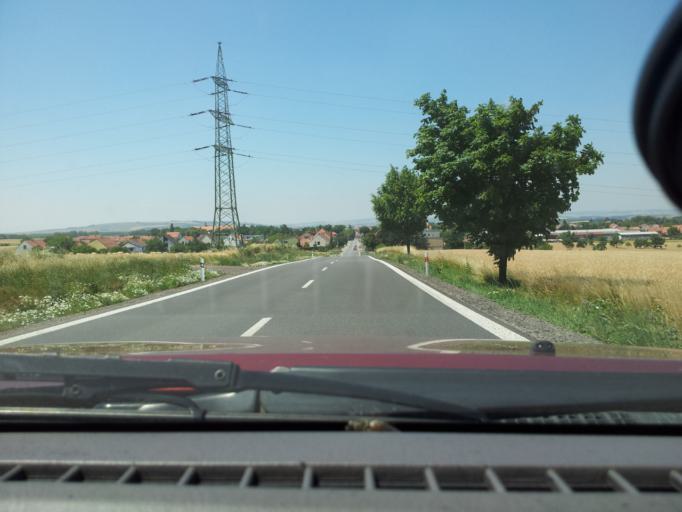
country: CZ
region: South Moravian
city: Tesany
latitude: 49.0373
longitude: 16.7807
